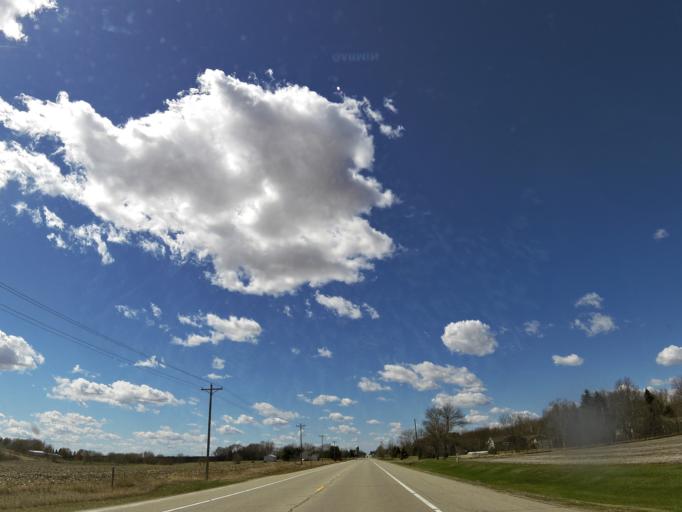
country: US
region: Minnesota
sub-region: Washington County
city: Cottage Grove
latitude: 44.7168
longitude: -92.9667
